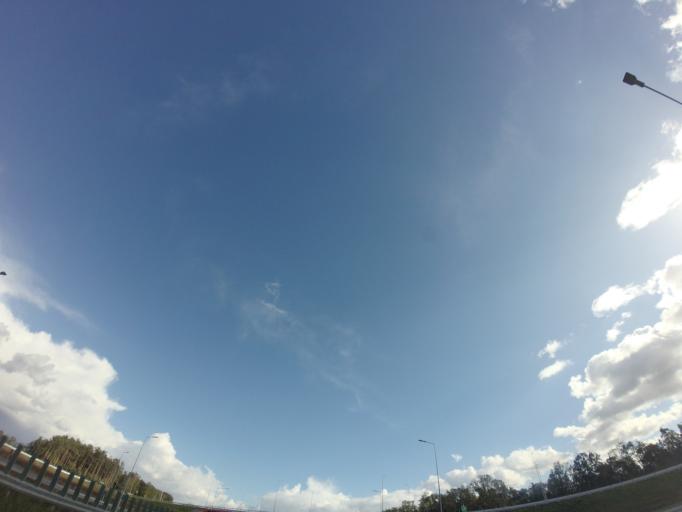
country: PL
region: Lubusz
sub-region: Powiat nowosolski
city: Nowe Miasteczko
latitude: 51.6830
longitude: 15.7607
